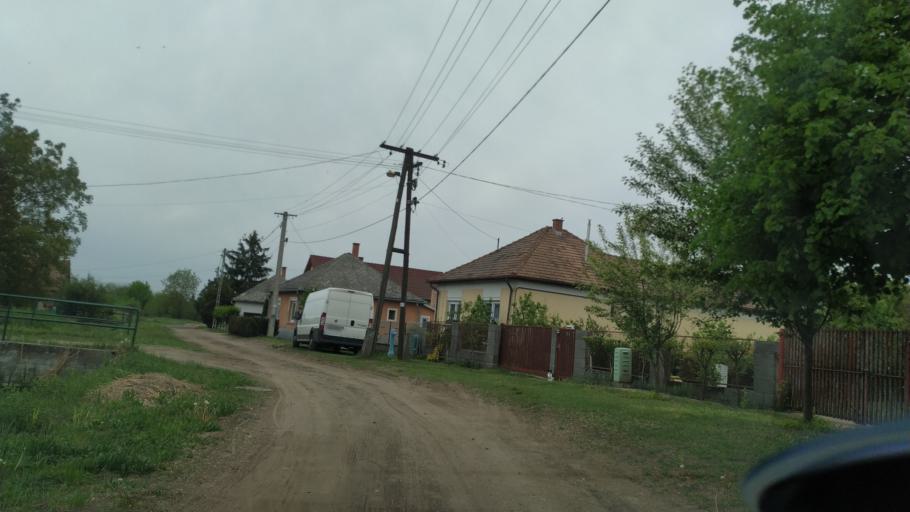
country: HU
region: Pest
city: Nagykata
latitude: 47.4125
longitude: 19.7281
